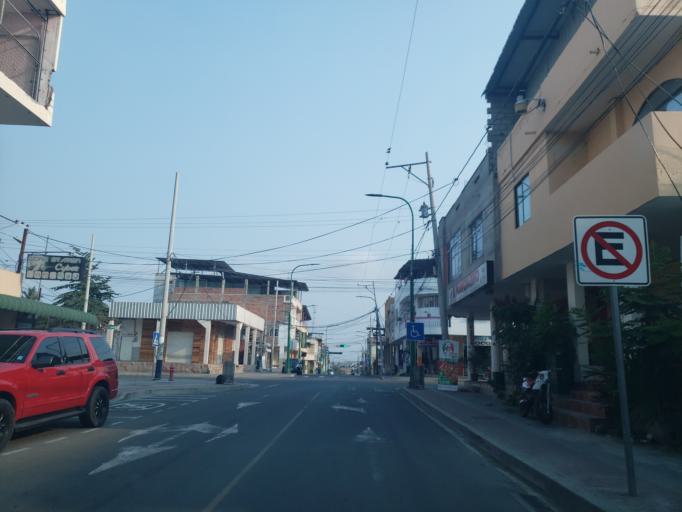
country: EC
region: Manabi
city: Manta
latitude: -0.9531
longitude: -80.7286
